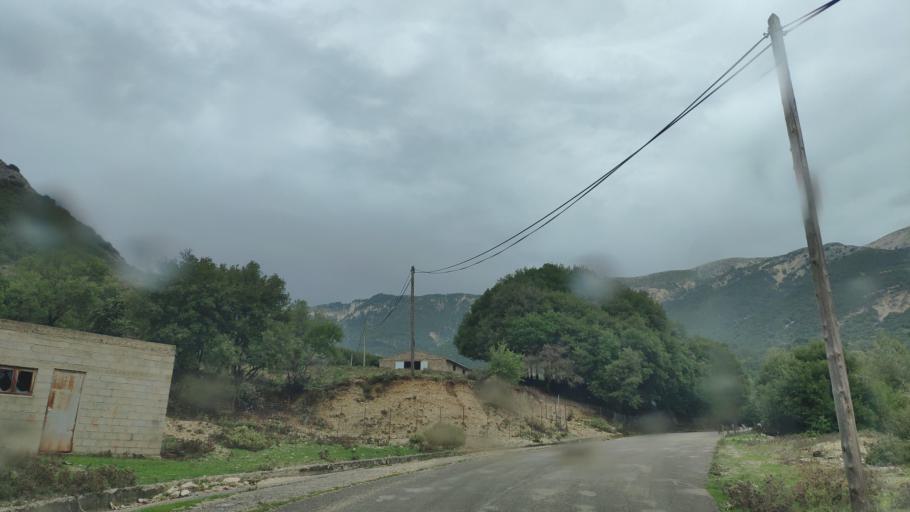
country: GR
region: Epirus
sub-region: Nomos Thesprotias
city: Paramythia
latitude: 39.4202
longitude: 20.6177
